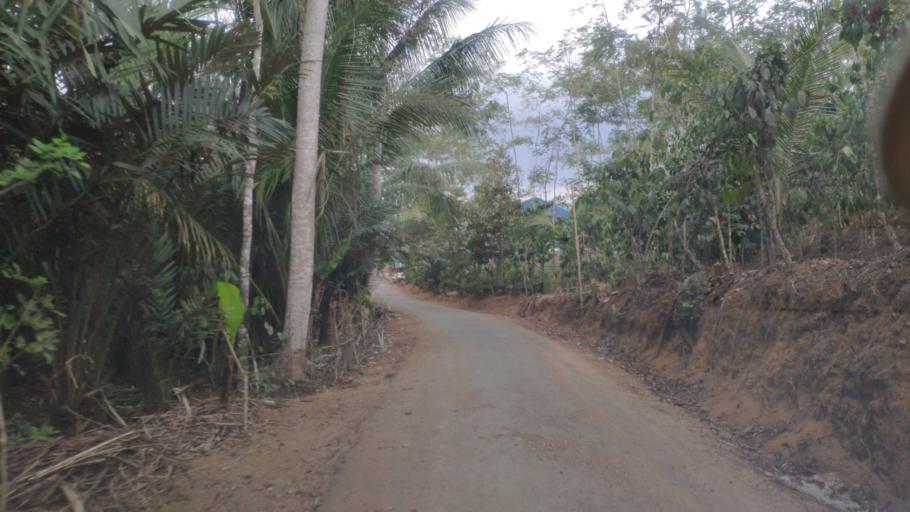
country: ID
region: Central Java
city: Wonosobo
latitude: -7.3357
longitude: 109.6568
